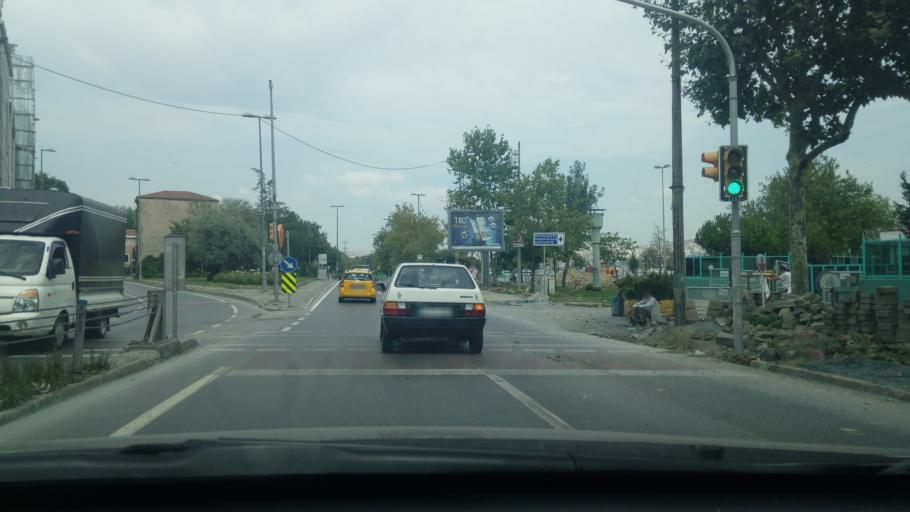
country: TR
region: Istanbul
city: Istanbul
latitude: 41.0295
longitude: 28.9518
